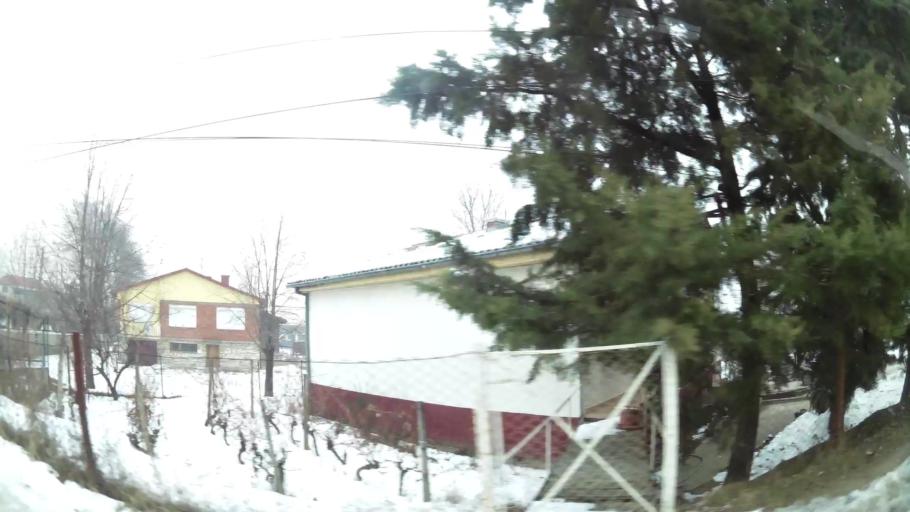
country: MK
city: Kondovo
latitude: 42.0491
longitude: 21.3436
